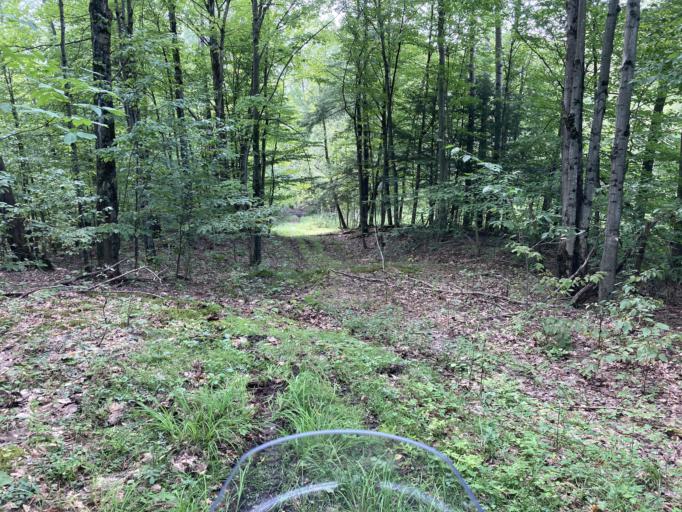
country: US
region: Vermont
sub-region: Franklin County
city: Enosburg Falls
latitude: 44.8175
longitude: -72.8860
